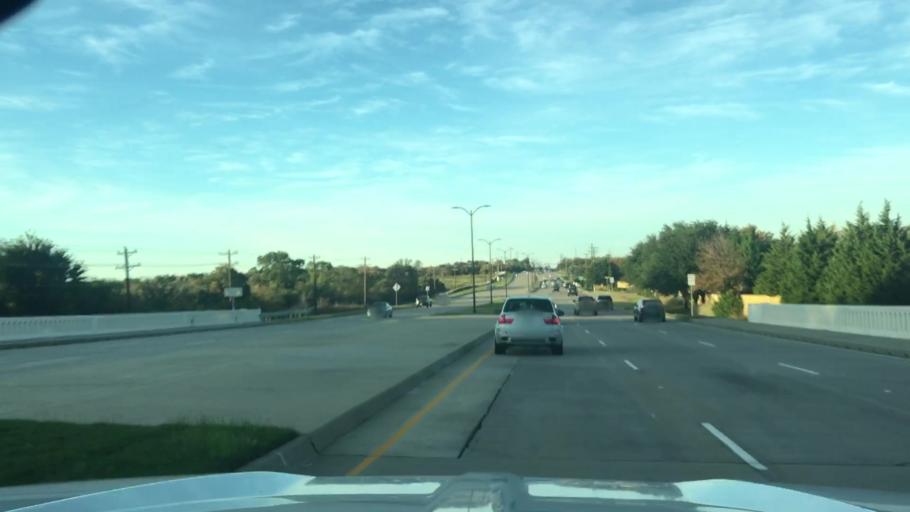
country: US
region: Texas
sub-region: Collin County
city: Frisco
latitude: 33.1757
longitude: -96.8030
